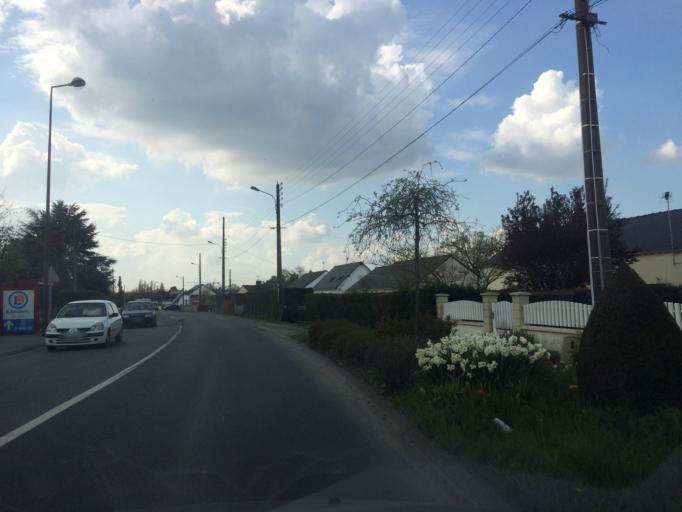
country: FR
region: Pays de la Loire
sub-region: Departement de la Loire-Atlantique
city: Blain
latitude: 47.4735
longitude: -1.7467
